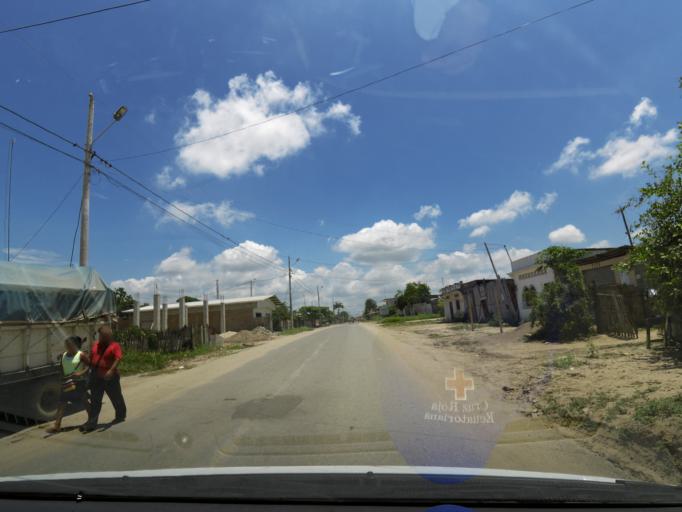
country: EC
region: El Oro
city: Huaquillas
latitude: -3.4813
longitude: -80.2121
